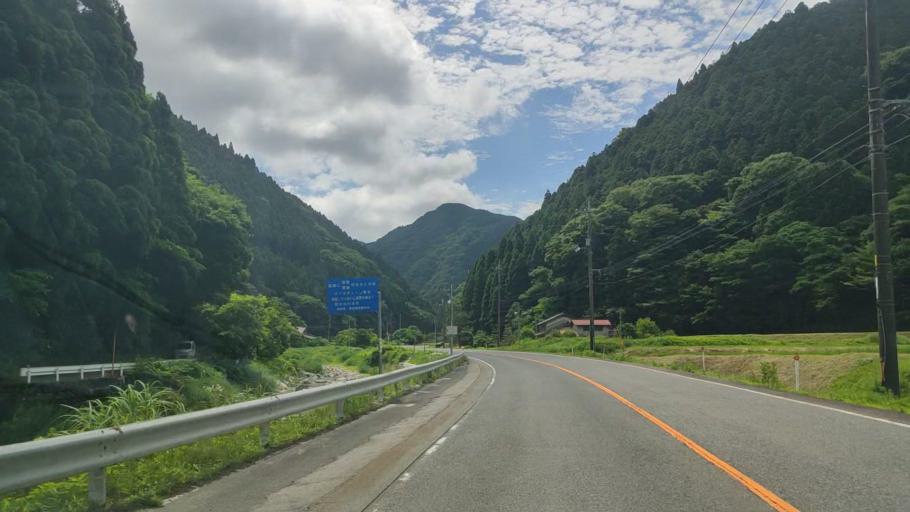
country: JP
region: Okayama
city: Niimi
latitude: 35.2153
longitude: 133.4613
